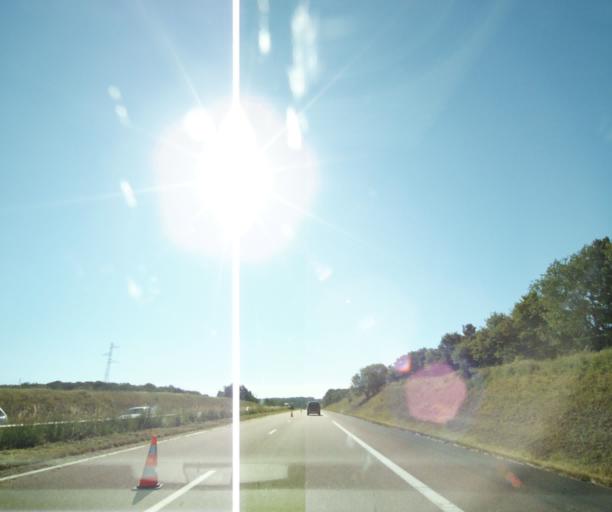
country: FR
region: Champagne-Ardenne
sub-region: Departement de l'Aube
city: Ville-sous-la-Ferte
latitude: 48.1257
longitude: 4.6949
